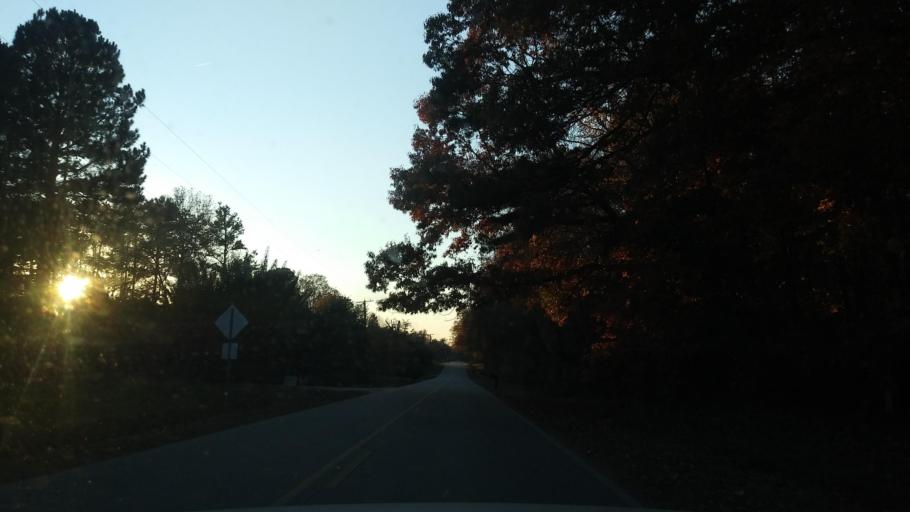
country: US
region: North Carolina
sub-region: Guilford County
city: Pleasant Garden
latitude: 36.0013
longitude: -79.7637
